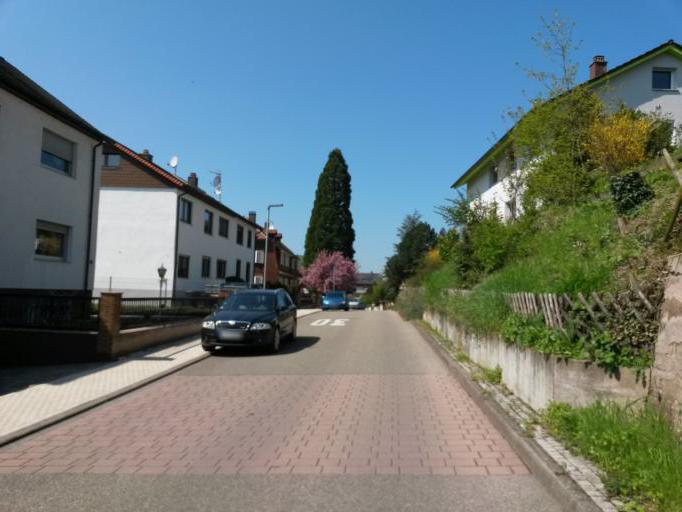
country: DE
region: Baden-Wuerttemberg
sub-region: Karlsruhe Region
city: Joehlingen
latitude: 48.9863
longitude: 8.5474
